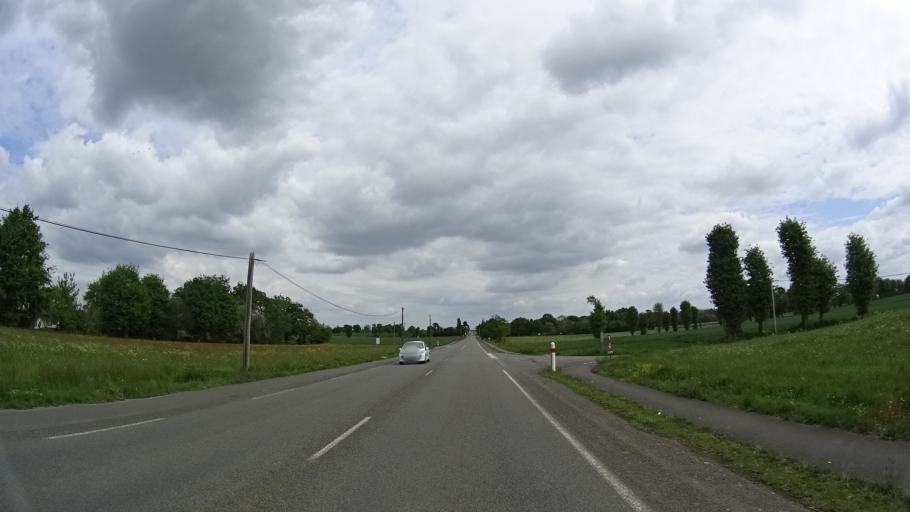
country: FR
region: Brittany
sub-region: Departement d'Ille-et-Vilaine
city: Mordelles
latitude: 48.0823
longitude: -1.8221
